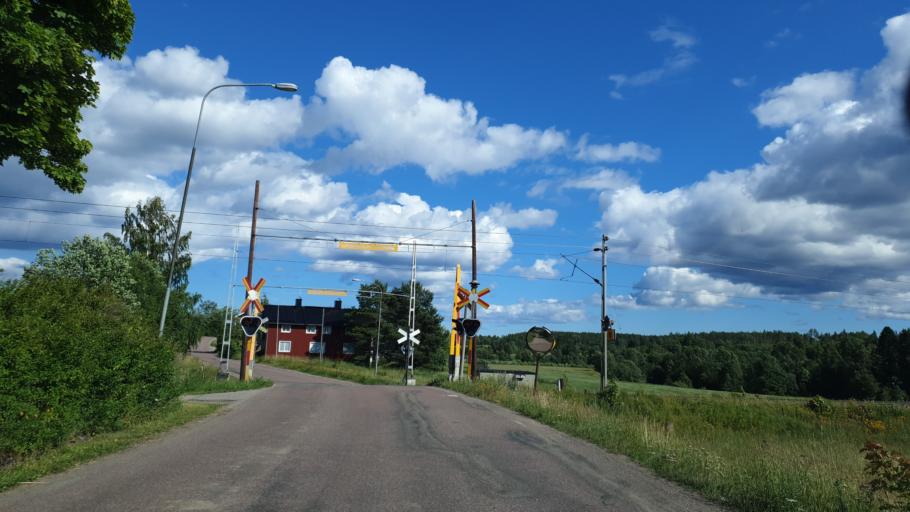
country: SE
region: Gaevleborg
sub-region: Nordanstigs Kommun
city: Bergsjoe
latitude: 62.0504
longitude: 17.2211
